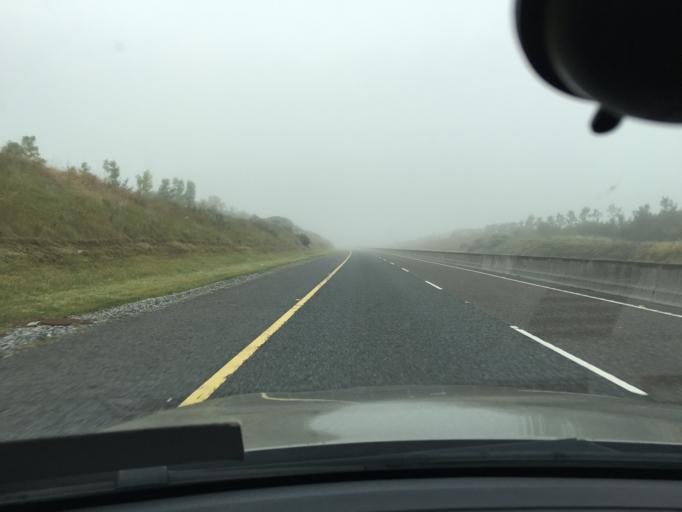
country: IE
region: Leinster
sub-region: Uibh Fhaili
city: Clara
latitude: 53.3846
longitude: -7.5849
